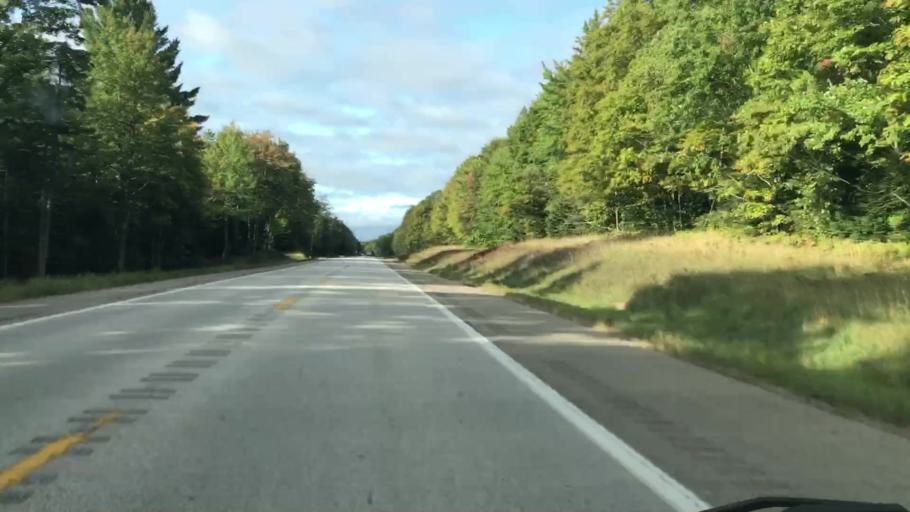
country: US
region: Michigan
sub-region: Luce County
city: Newberry
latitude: 46.3405
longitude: -85.0399
